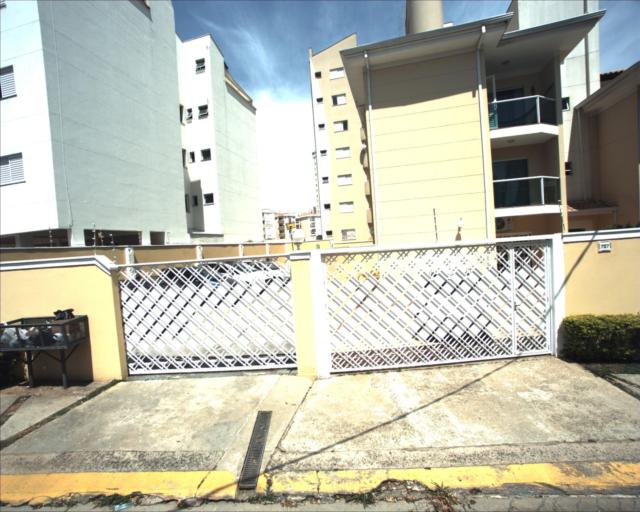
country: BR
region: Sao Paulo
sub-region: Sorocaba
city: Sorocaba
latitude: -23.5324
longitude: -47.4680
